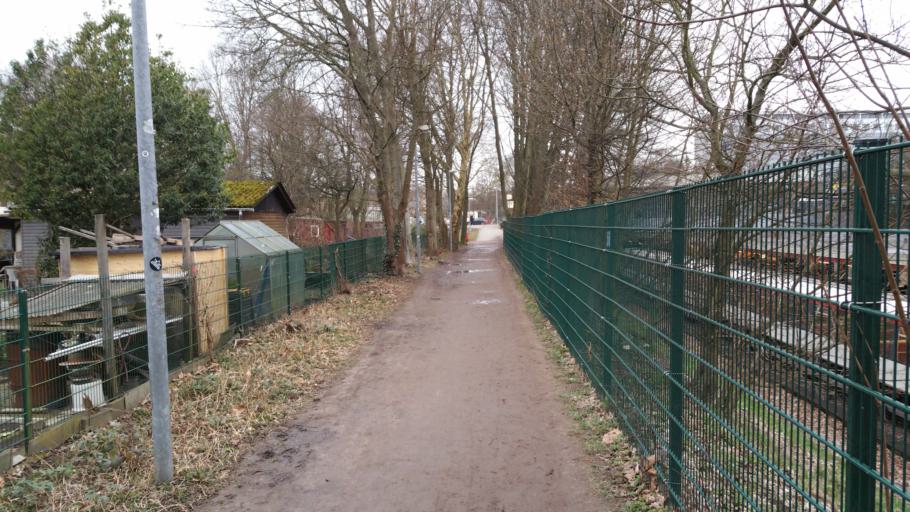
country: DE
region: Hamburg
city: Stellingen
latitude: 53.5922
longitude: 9.9439
